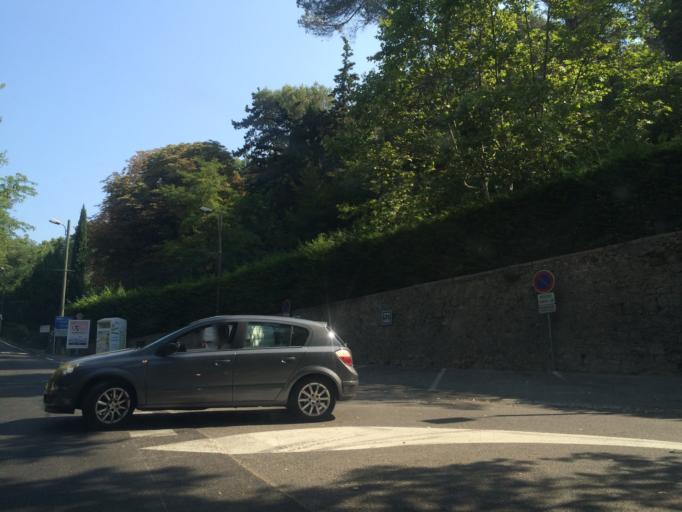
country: FR
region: Provence-Alpes-Cote d'Azur
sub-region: Departement des Alpes-Maritimes
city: Saint-Paul-de-Vence
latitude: 43.7020
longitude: 7.1169
